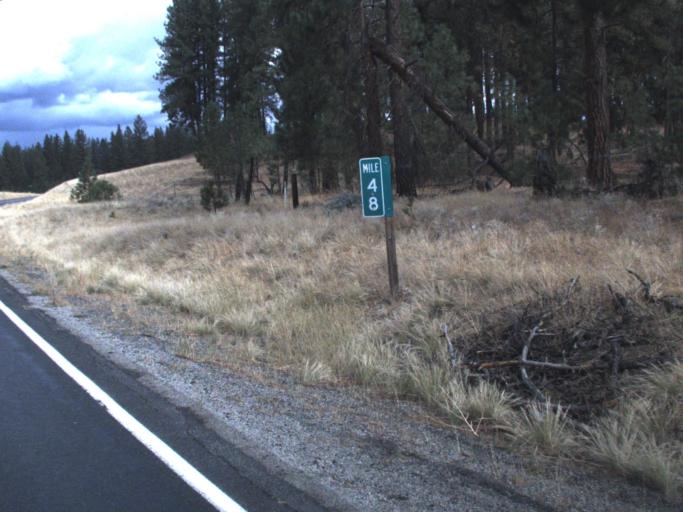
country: US
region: Washington
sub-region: Spokane County
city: Fairchild Air Force Base
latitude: 47.8826
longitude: -117.8394
